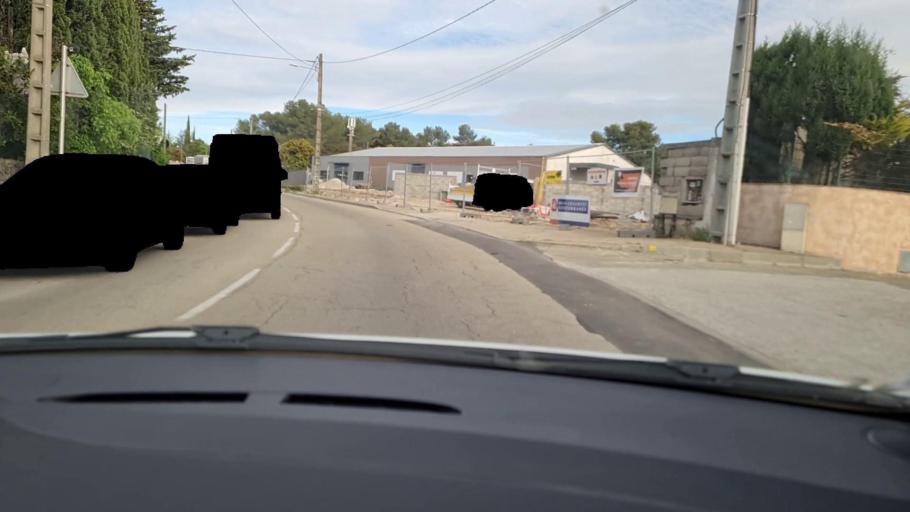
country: FR
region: Languedoc-Roussillon
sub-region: Departement du Gard
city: Nimes
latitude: 43.8424
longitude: 4.3127
